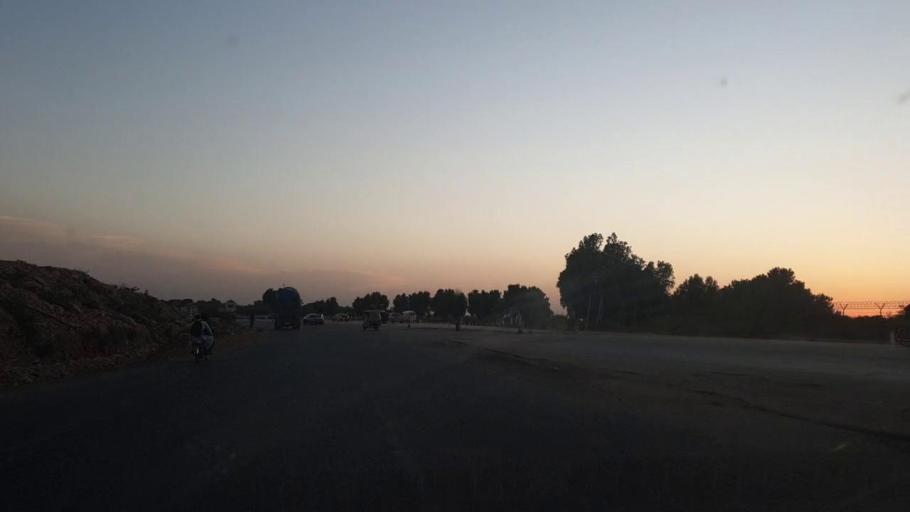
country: PK
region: Sindh
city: Jamshoro
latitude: 25.4091
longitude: 68.2677
